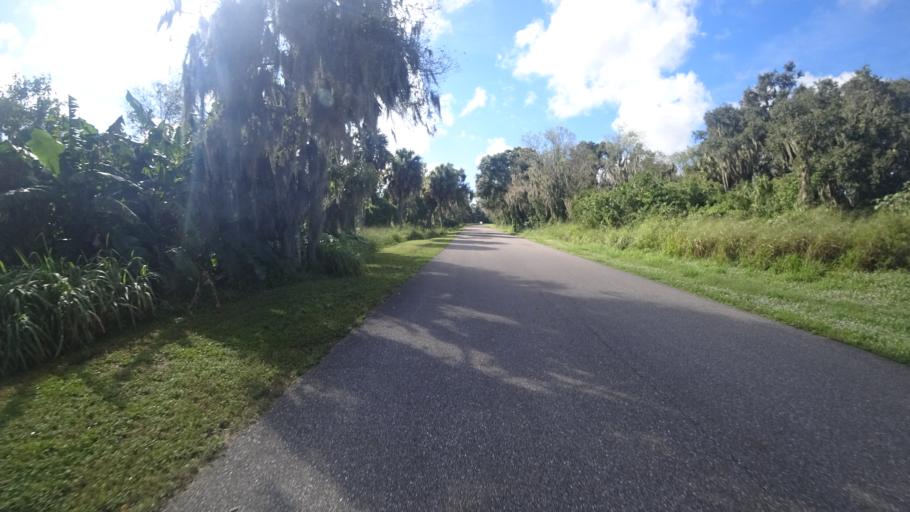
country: US
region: Florida
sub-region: Manatee County
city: Ellenton
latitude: 27.5759
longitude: -82.4748
